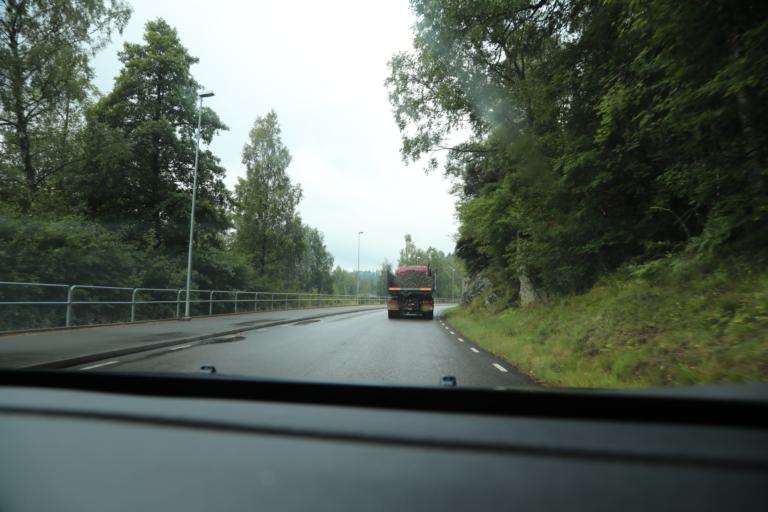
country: SE
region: Halland
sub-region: Halmstads Kommun
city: Getinge
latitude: 57.1306
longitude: 12.7118
